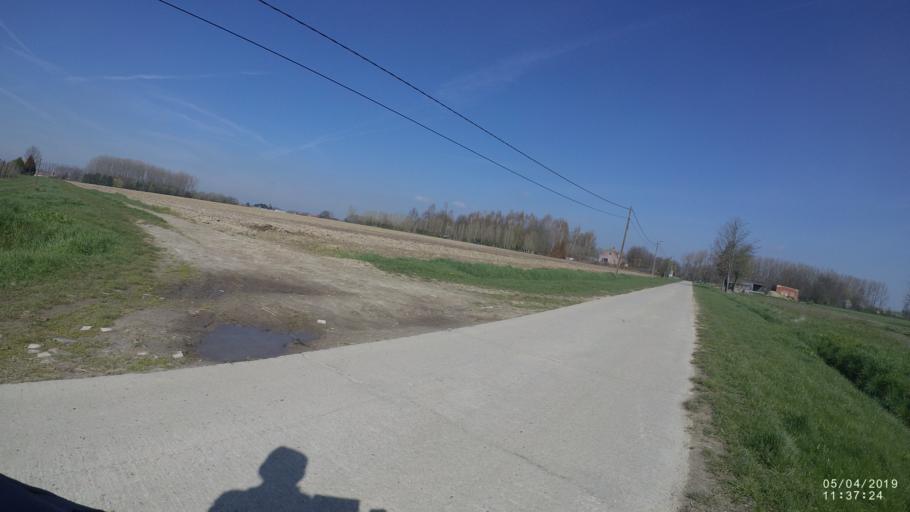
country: BE
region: Flanders
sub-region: Provincie Limburg
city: Nieuwerkerken
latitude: 50.8970
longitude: 5.1684
